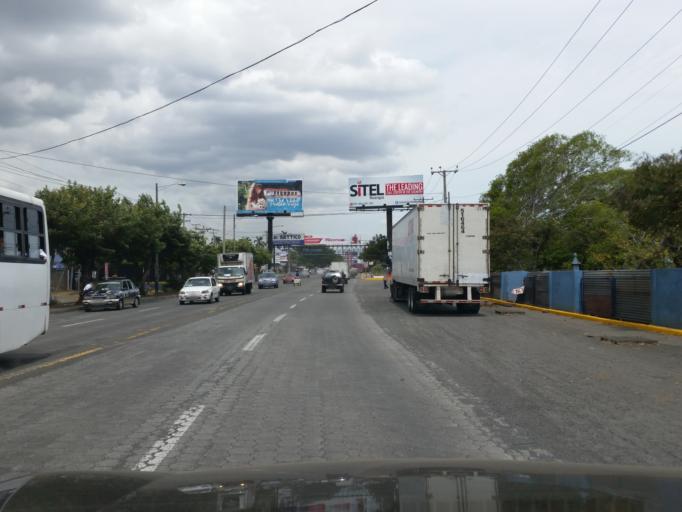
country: NI
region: Managua
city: Managua
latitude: 12.1303
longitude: -86.2628
